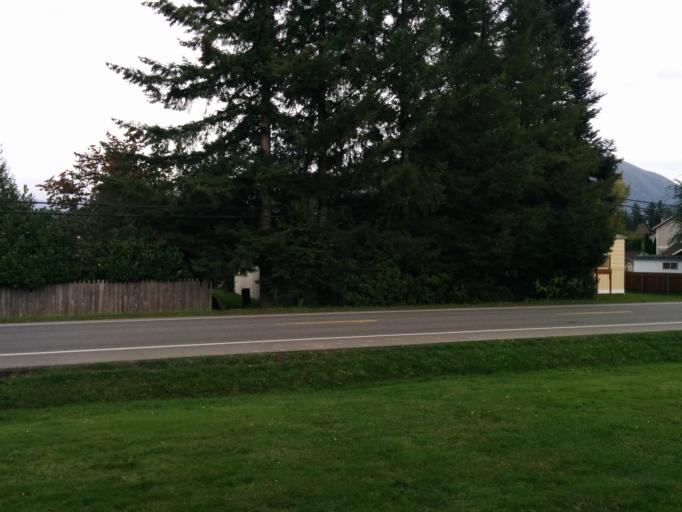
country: US
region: Washington
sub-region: King County
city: Snoqualmie
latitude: 47.5220
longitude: -121.8205
